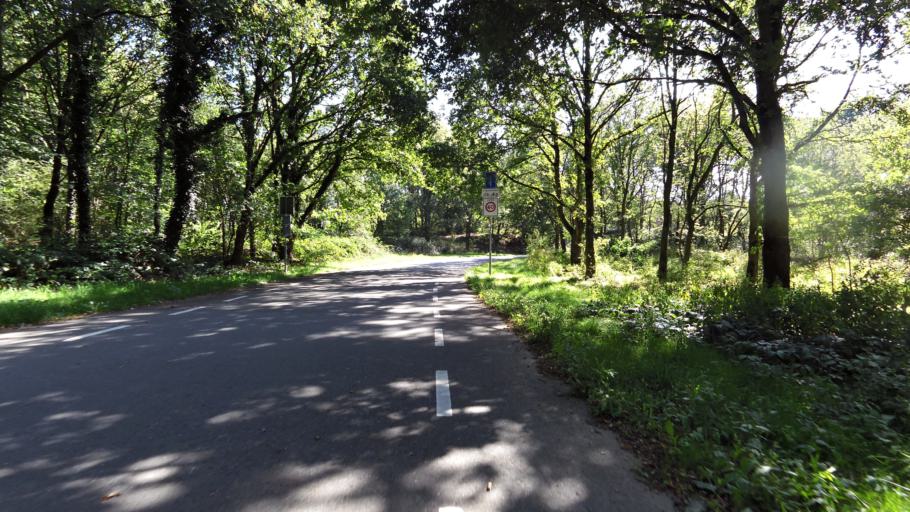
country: NL
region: Gelderland
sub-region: Gemeente Renkum
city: Heelsum
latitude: 51.9762
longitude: 5.7591
